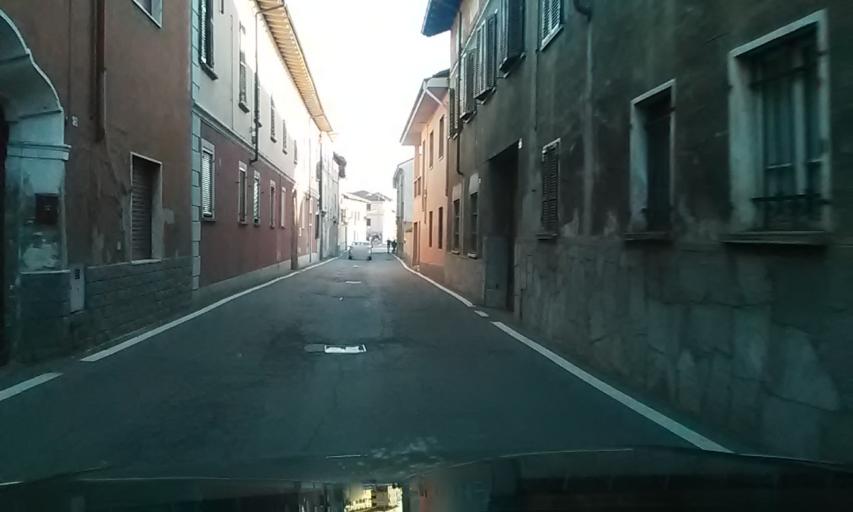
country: IT
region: Piedmont
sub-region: Provincia di Novara
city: Fara Novarese
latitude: 45.5527
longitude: 8.4599
